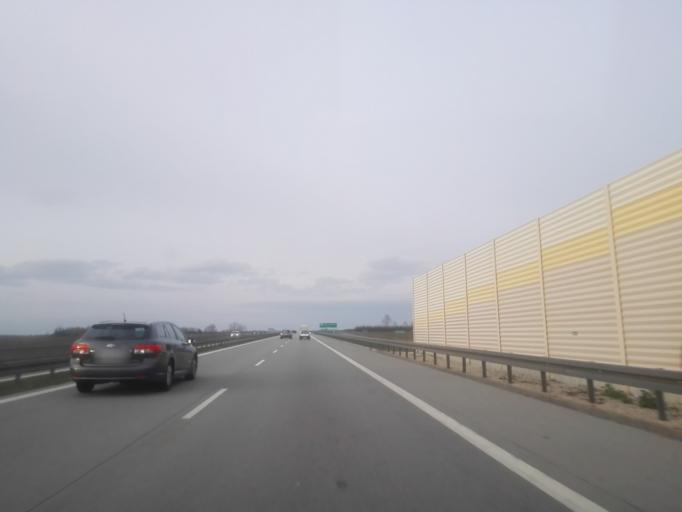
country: PL
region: Lodz Voivodeship
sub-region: Powiat skierniewicki
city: Kowiesy
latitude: 51.9032
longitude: 20.4362
